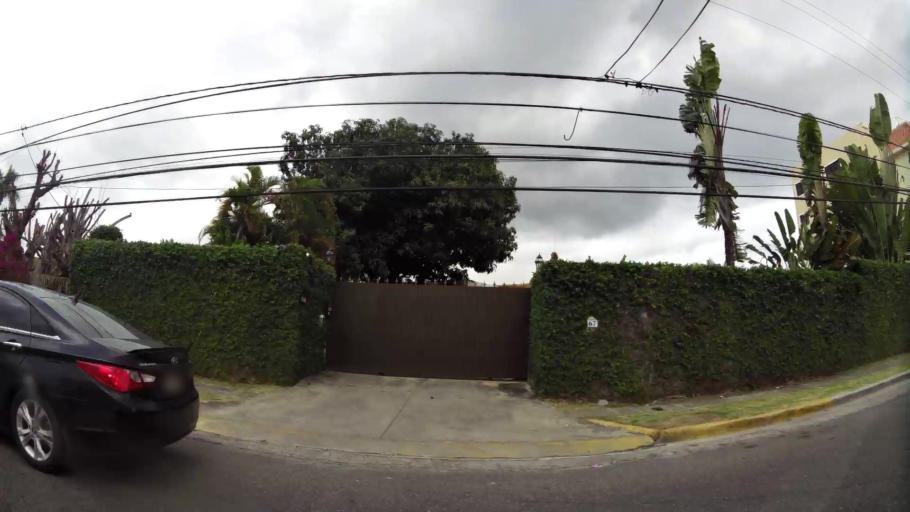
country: DO
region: Nacional
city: La Agustina
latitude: 18.4942
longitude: -69.9346
